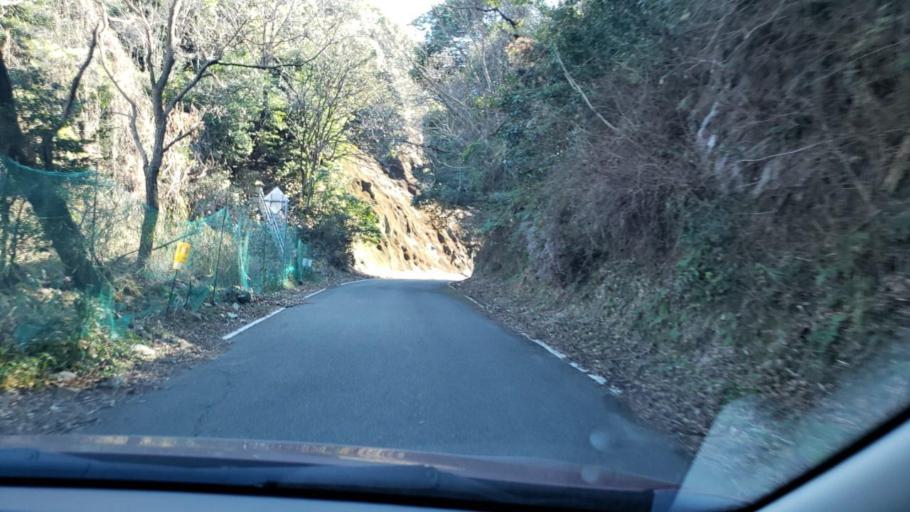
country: JP
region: Tokushima
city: Narutocho-mitsuishi
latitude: 34.1969
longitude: 134.5534
